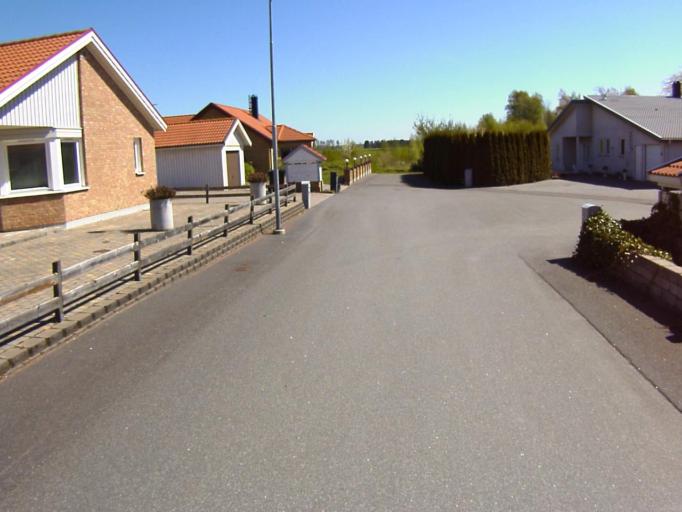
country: SE
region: Skane
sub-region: Kristianstads Kommun
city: Fjalkinge
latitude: 56.0495
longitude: 14.2179
